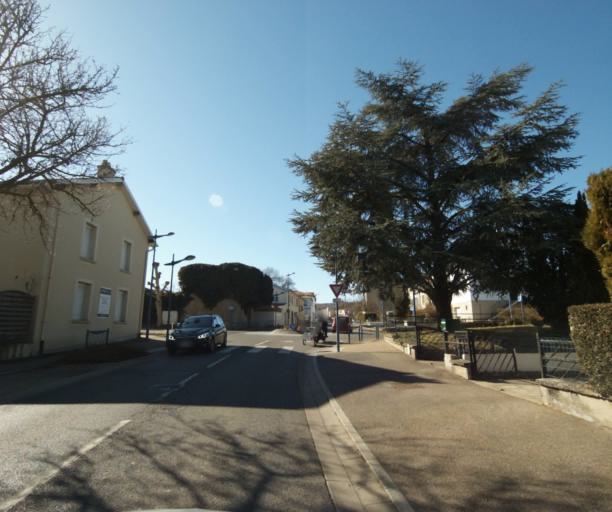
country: FR
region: Lorraine
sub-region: Departement de Meurthe-et-Moselle
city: Heillecourt
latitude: 48.6540
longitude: 6.1981
